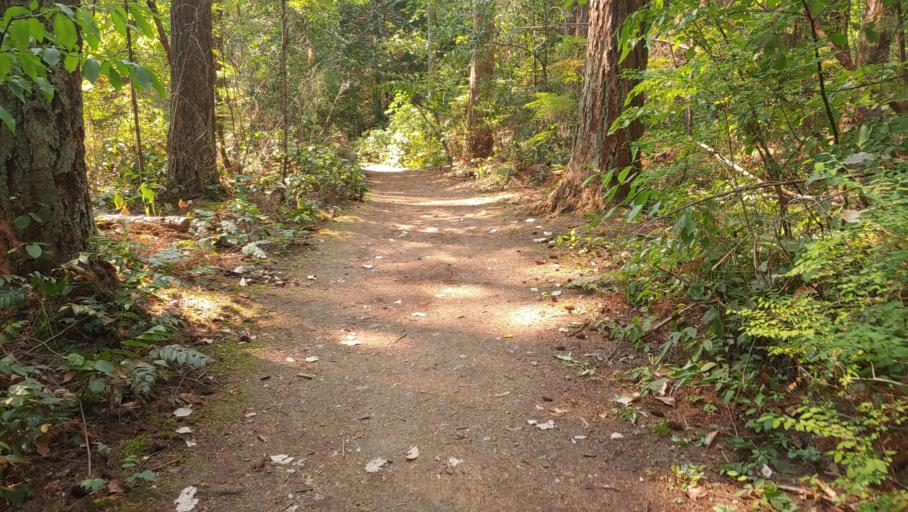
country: US
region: Washington
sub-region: King County
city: Eastgate
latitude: 47.5866
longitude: -122.1403
